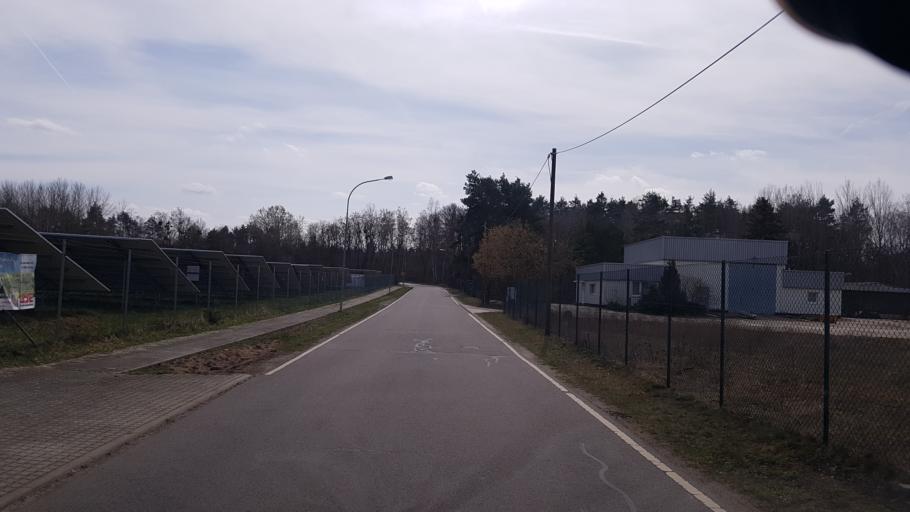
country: DE
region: Brandenburg
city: Schipkau
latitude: 51.5108
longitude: 13.8905
